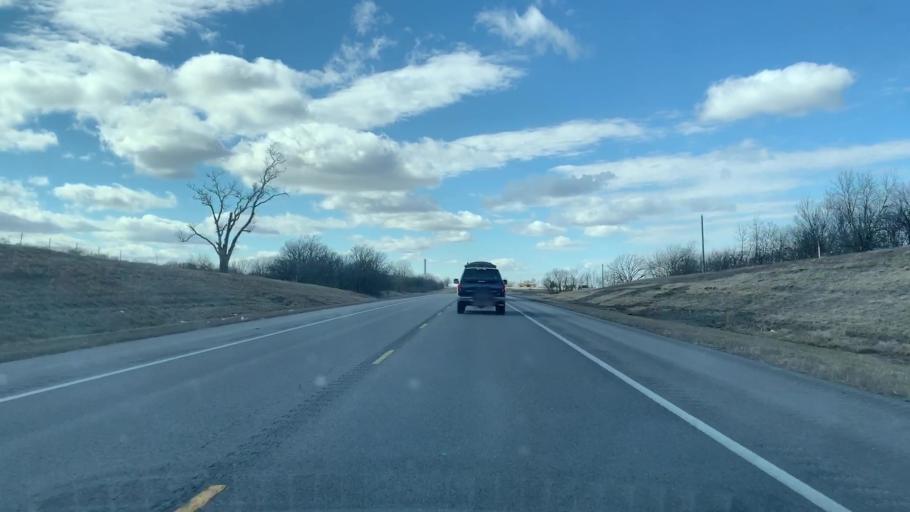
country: US
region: Kansas
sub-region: Cherokee County
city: Columbus
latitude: 37.3400
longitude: -94.8967
